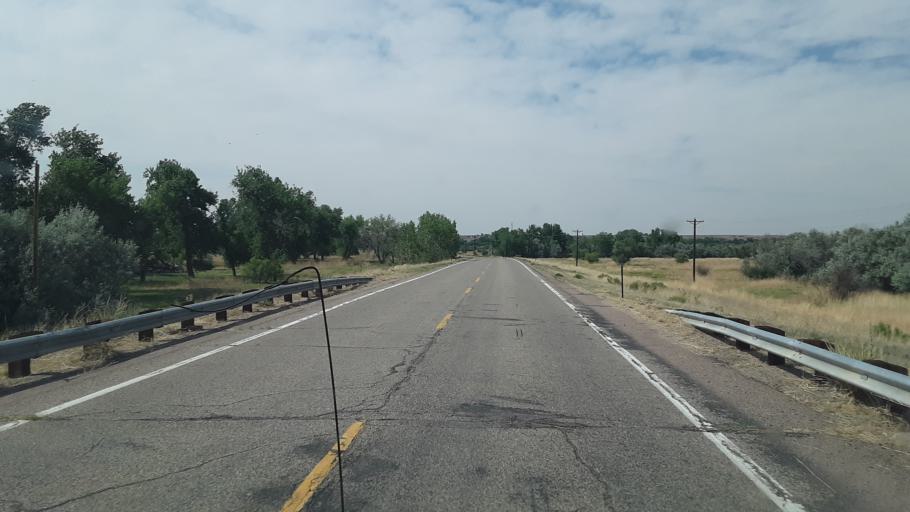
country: US
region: Colorado
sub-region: Otero County
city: Fowler
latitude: 38.2341
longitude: -104.2613
